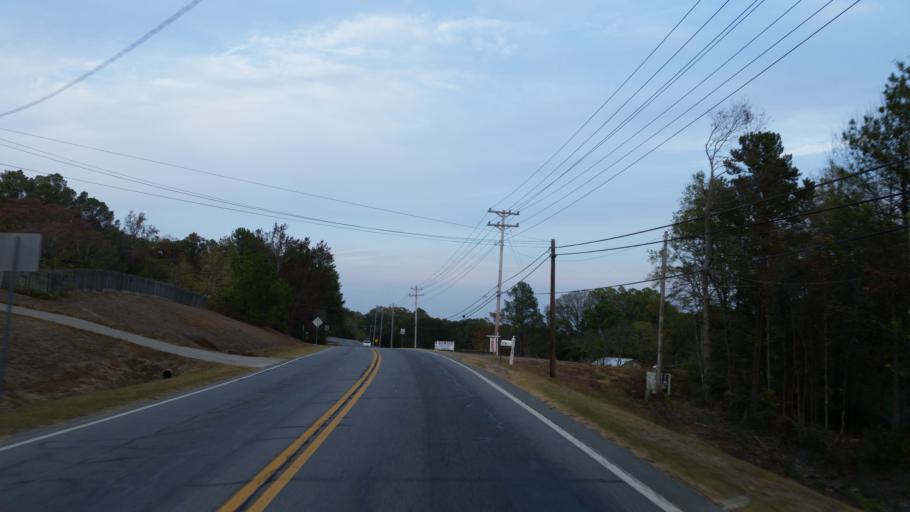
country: US
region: Georgia
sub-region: Gordon County
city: Calhoun
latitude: 34.5868
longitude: -84.9362
